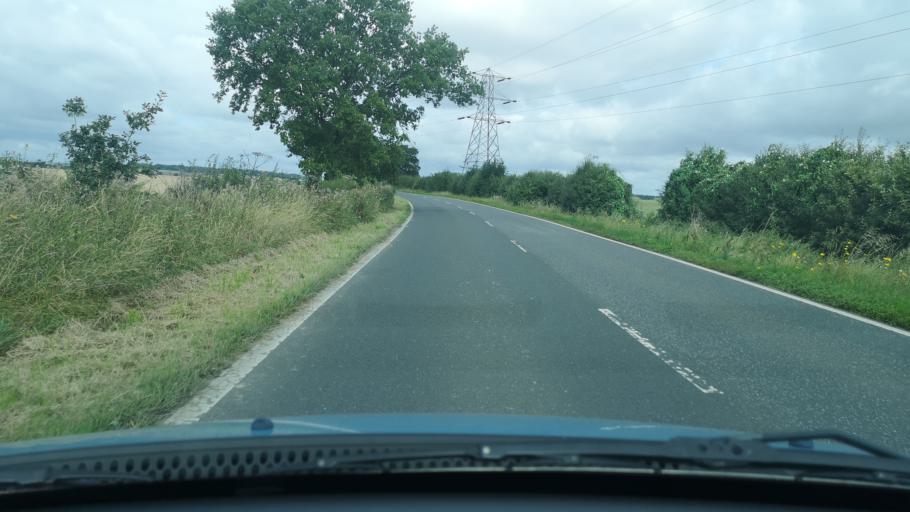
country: GB
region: England
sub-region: Barnsley
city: Royston
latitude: 53.6184
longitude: -1.4420
